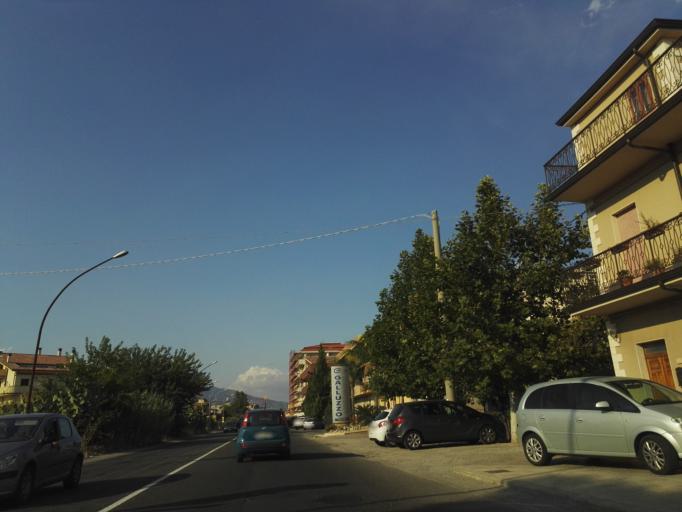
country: IT
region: Calabria
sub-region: Provincia di Reggio Calabria
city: Siderno
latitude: 38.2833
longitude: 16.3125
